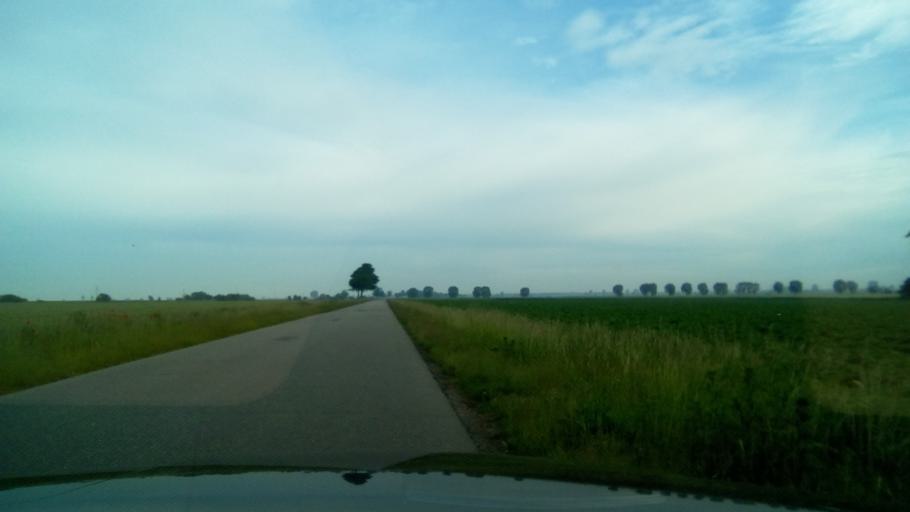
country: PL
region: Greater Poland Voivodeship
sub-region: Powiat gnieznienski
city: Mieleszyn
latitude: 52.6118
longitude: 17.5410
